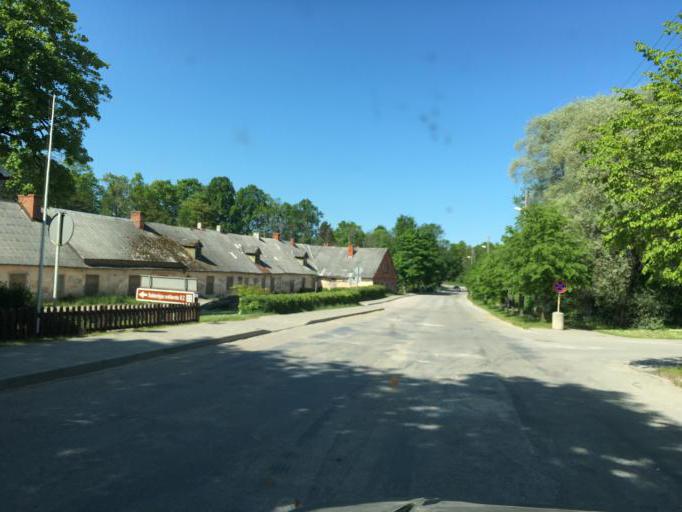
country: LV
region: Dundaga
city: Dundaga
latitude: 57.5109
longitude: 22.3517
